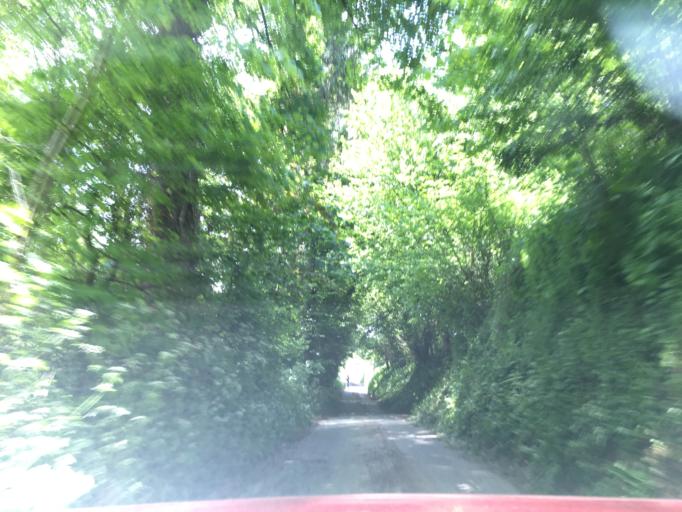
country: GB
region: England
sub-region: Gloucestershire
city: Dursley
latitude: 51.6619
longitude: -2.3474
